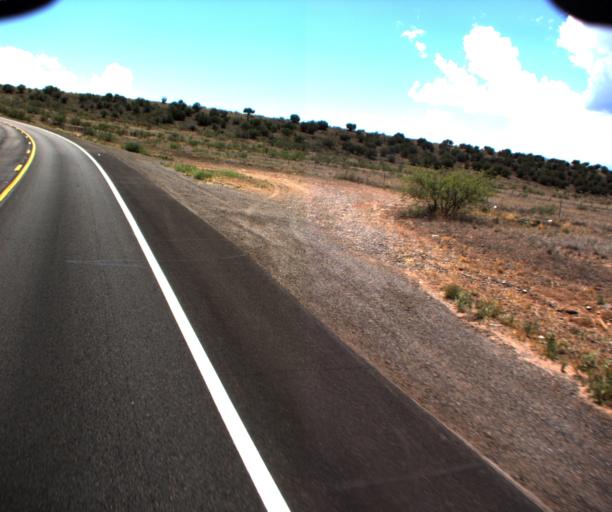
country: US
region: Arizona
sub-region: Yavapai County
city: Camp Verde
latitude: 34.5113
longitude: -111.7727
